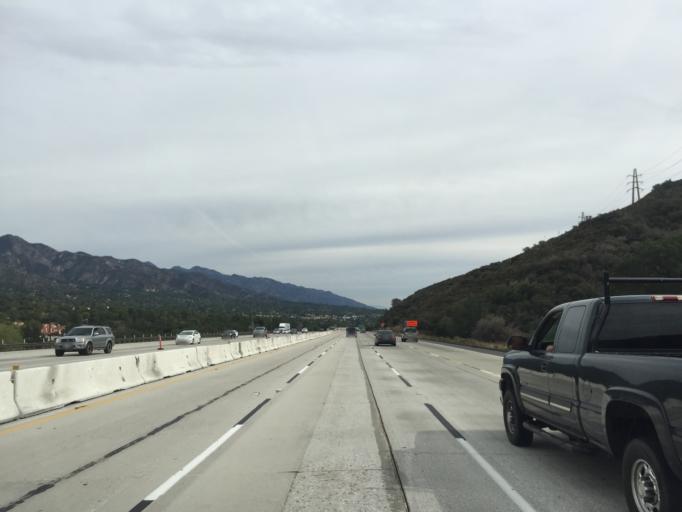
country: US
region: California
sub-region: Los Angeles County
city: La Crescenta-Montrose
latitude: 34.2333
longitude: -118.2762
